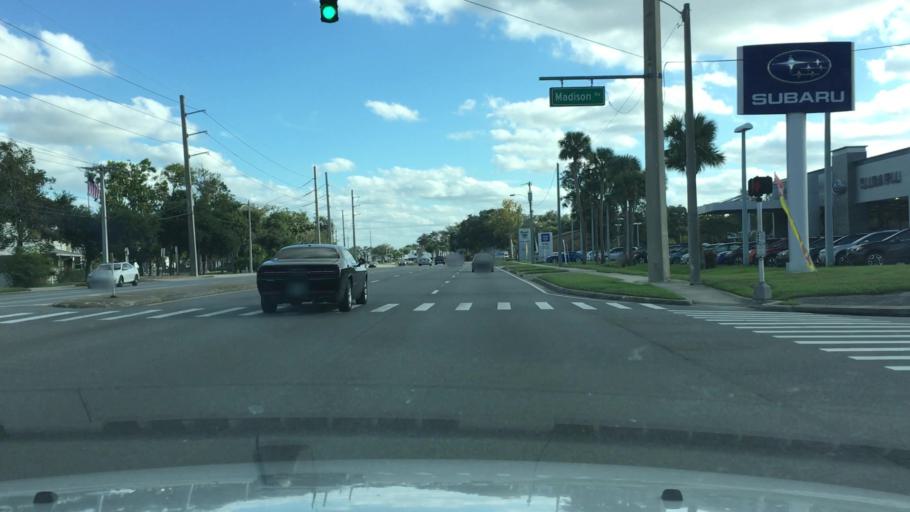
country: US
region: Florida
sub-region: Volusia County
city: Daytona Beach
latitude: 29.2167
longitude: -81.0465
